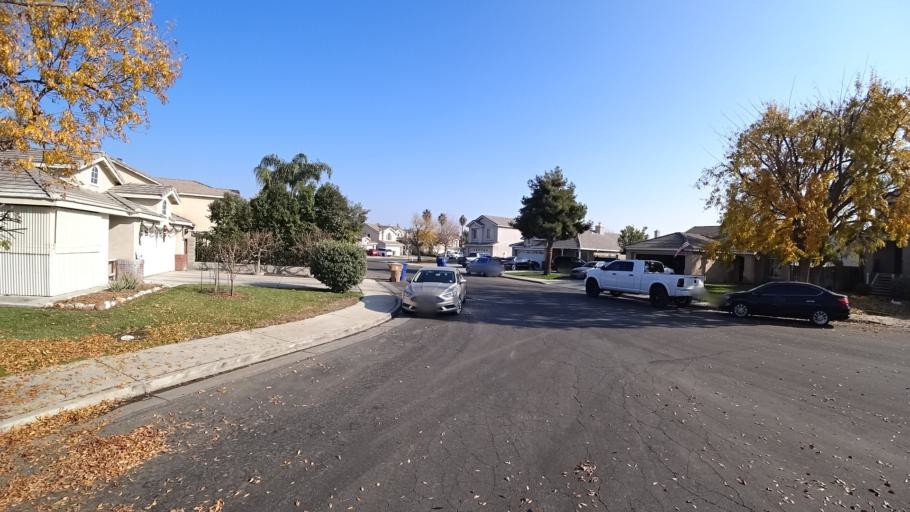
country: US
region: California
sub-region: Kern County
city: Greenacres
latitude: 35.3211
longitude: -119.0957
